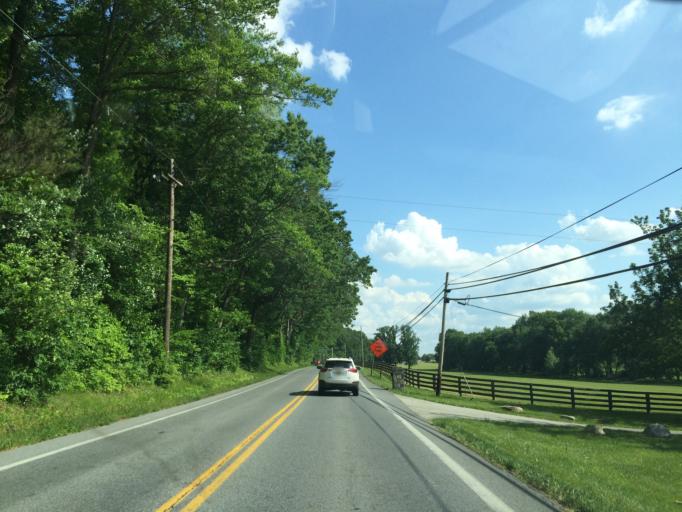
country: US
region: Maryland
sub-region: Carroll County
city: Sykesville
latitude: 39.3264
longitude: -76.8988
